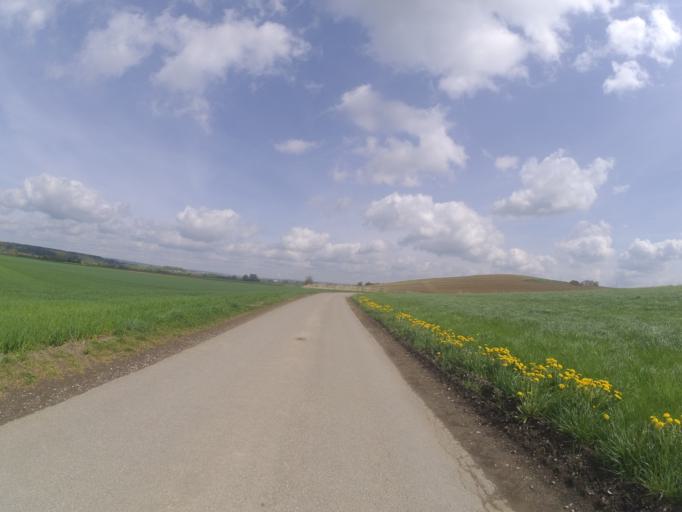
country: DE
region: Baden-Wuerttemberg
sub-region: Tuebingen Region
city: Rottenacker
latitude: 48.2246
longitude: 9.7200
